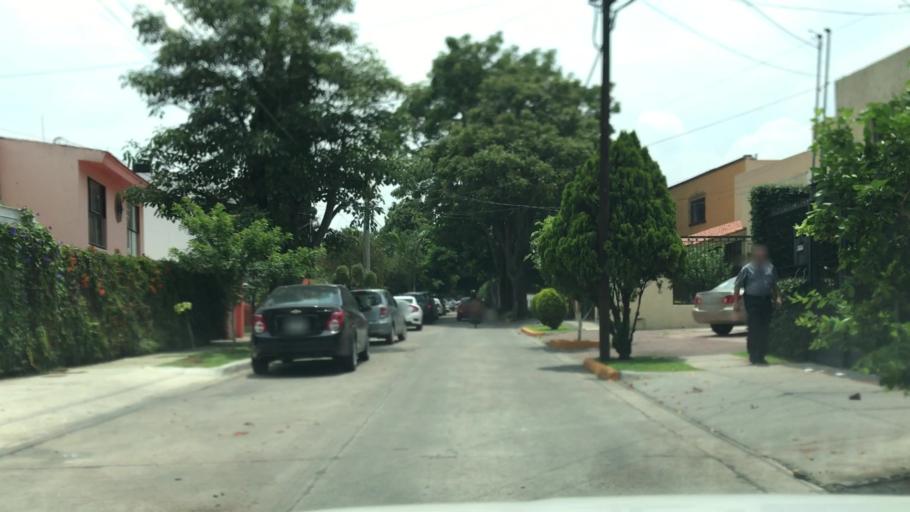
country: MX
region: Jalisco
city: Guadalajara
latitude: 20.6648
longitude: -103.4068
